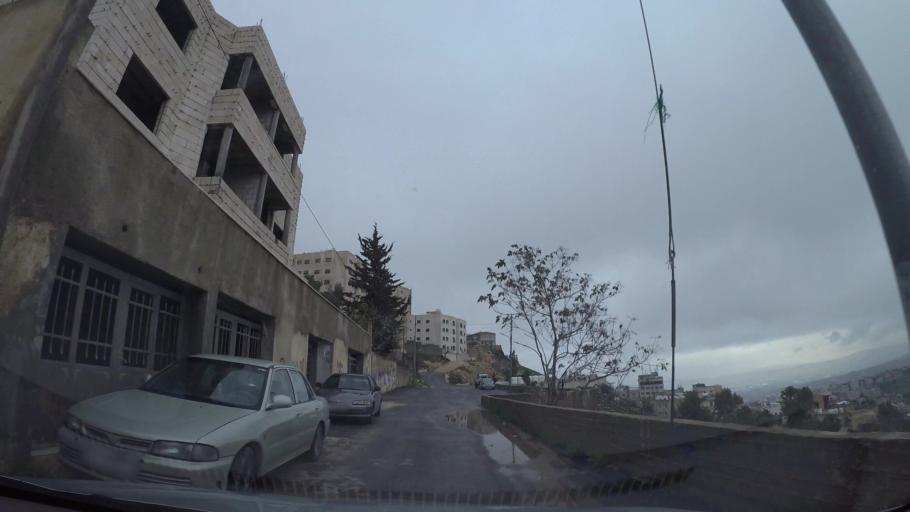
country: JO
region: Amman
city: Al Jubayhah
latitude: 32.0236
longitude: 35.8375
